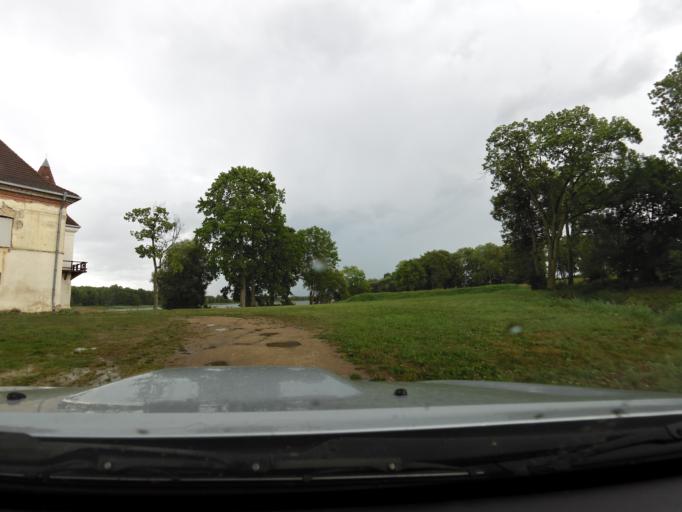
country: LT
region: Vilnius County
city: Ukmerge
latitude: 55.2860
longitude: 24.5138
